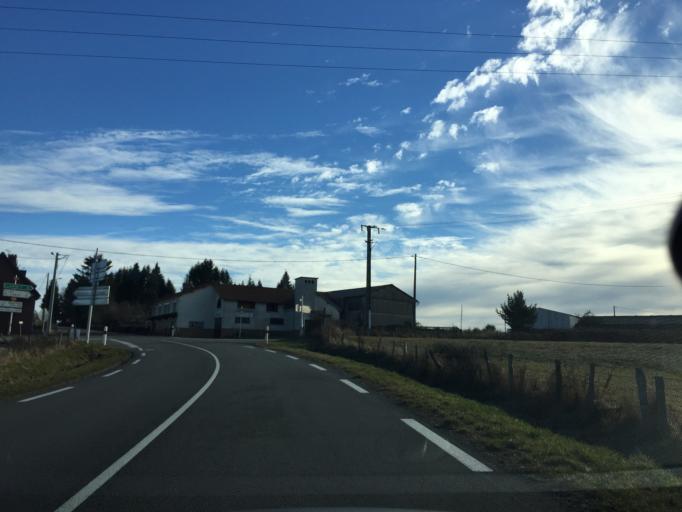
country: FR
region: Limousin
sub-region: Departement de la Creuse
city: Auzances
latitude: 45.8886
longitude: 2.4808
